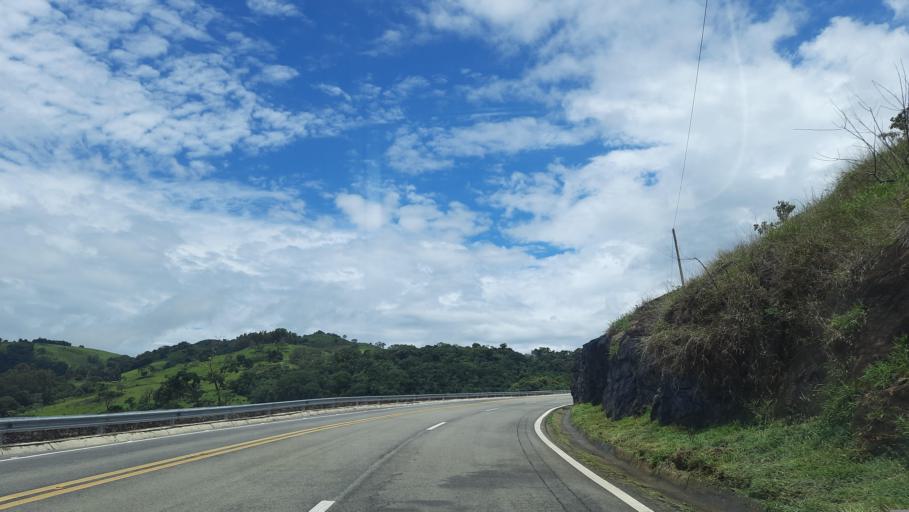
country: BR
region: Sao Paulo
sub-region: Vargem Grande Do Sul
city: Vargem Grande do Sul
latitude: -21.8320
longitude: -46.7558
